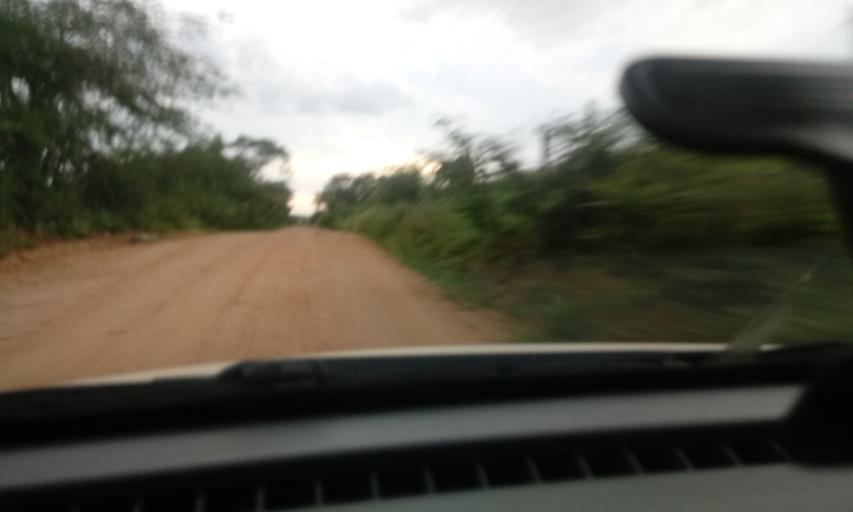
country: BR
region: Bahia
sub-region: Riacho De Santana
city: Riacho de Santana
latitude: -13.7941
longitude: -42.7321
